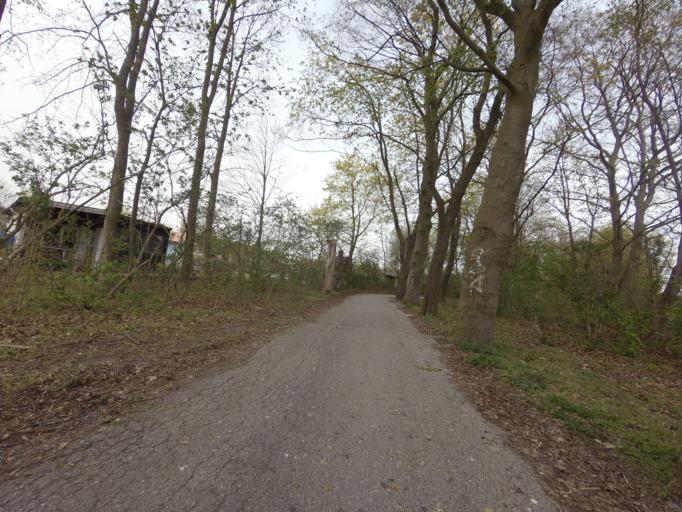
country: SE
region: Skane
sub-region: Lunds Kommun
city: Lund
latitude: 55.7214
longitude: 13.1707
